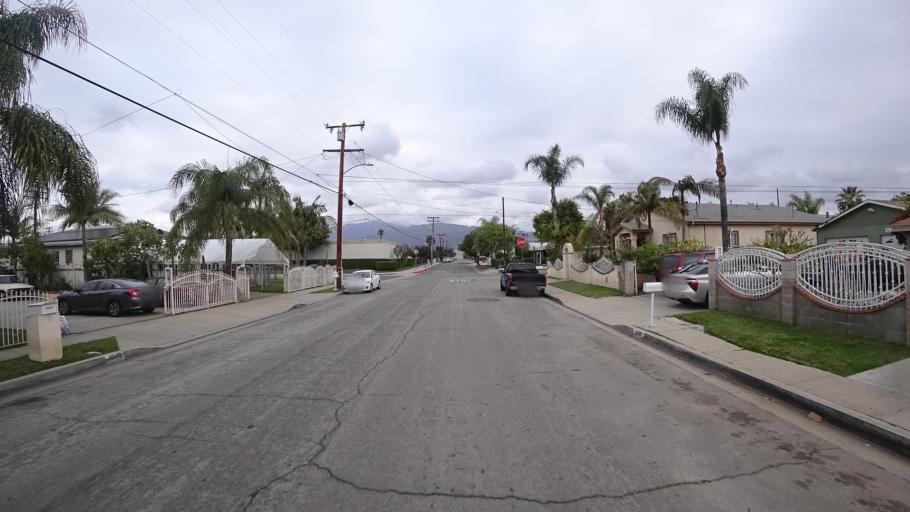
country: US
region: California
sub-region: Los Angeles County
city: Irwindale
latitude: 34.1029
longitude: -117.9463
